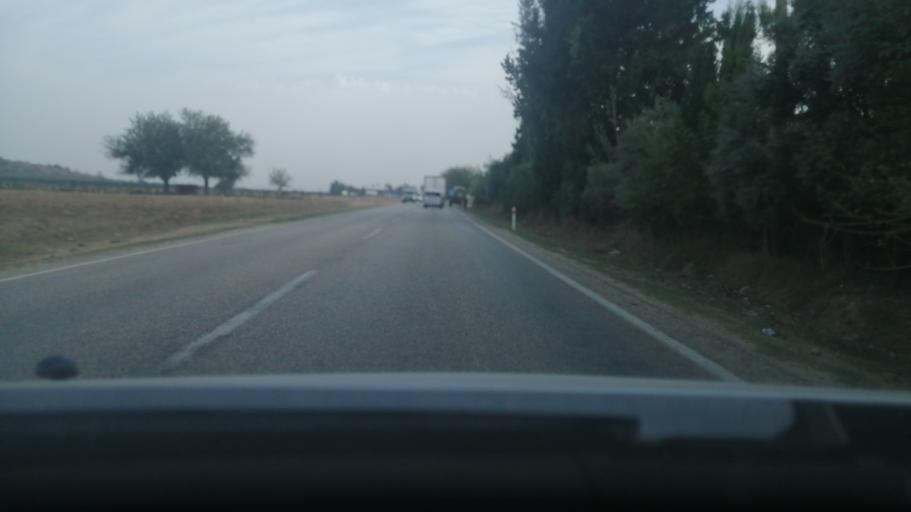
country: TR
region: Adana
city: Kozan
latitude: 37.3737
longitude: 35.8388
